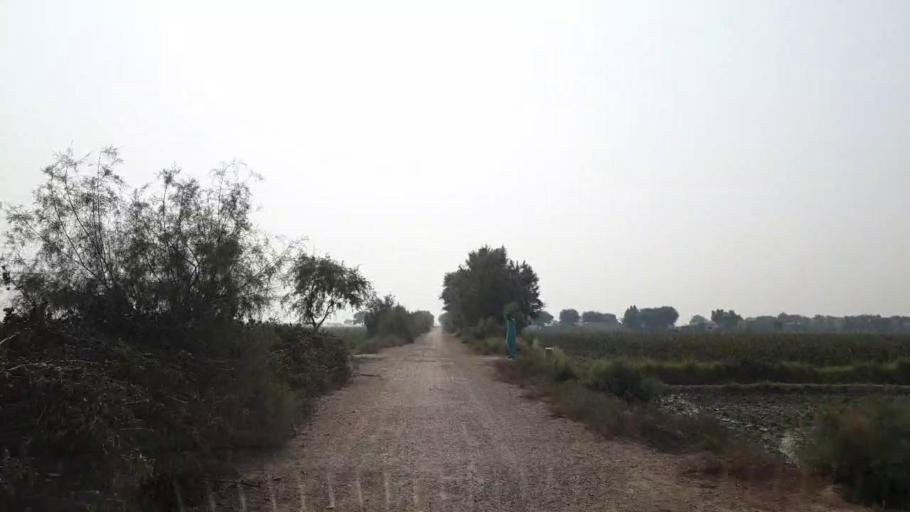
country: PK
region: Sindh
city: Bhan
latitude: 26.4682
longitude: 67.7390
